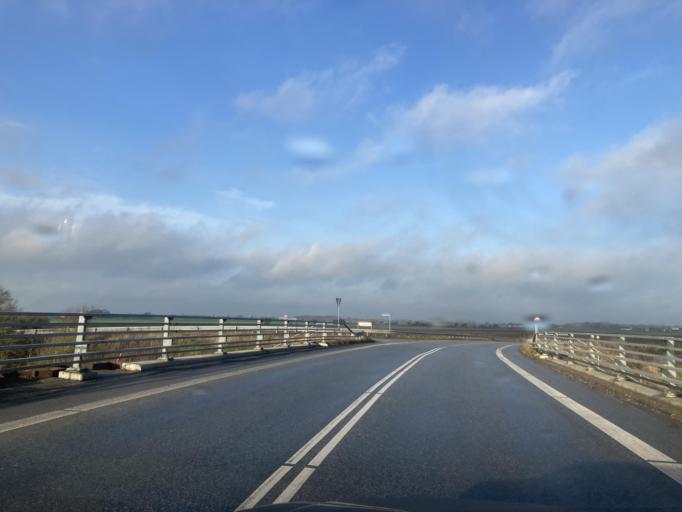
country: DK
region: Zealand
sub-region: Lolland Kommune
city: Rodby
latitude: 54.6789
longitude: 11.4250
